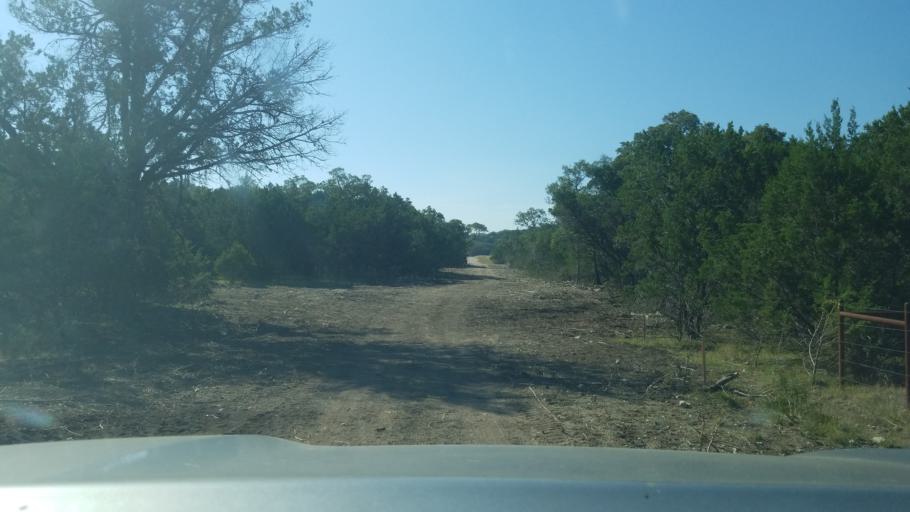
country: US
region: Texas
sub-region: Kendall County
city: Boerne
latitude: 29.7621
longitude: -98.7196
